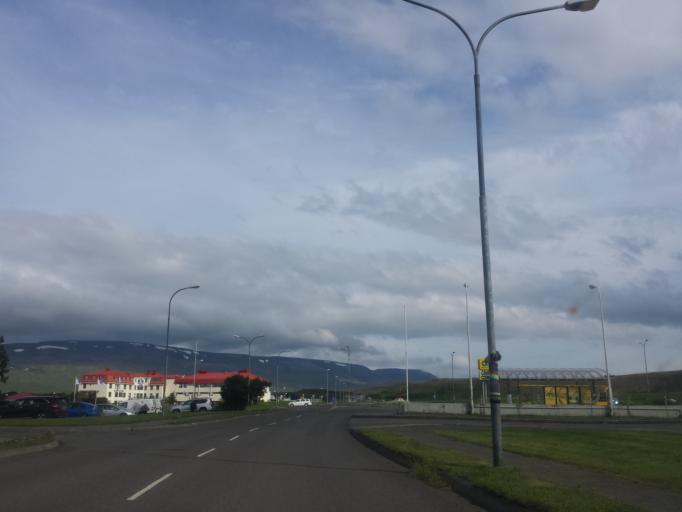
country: IS
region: Northwest
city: Saudarkrokur
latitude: 65.6567
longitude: -20.2862
